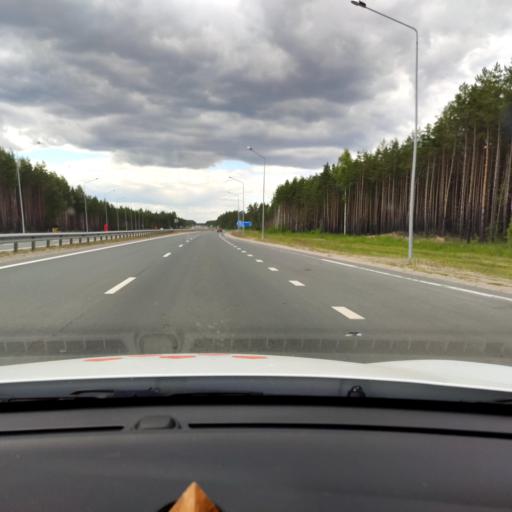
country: RU
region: Mariy-El
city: Surok
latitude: 56.4481
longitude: 48.1045
